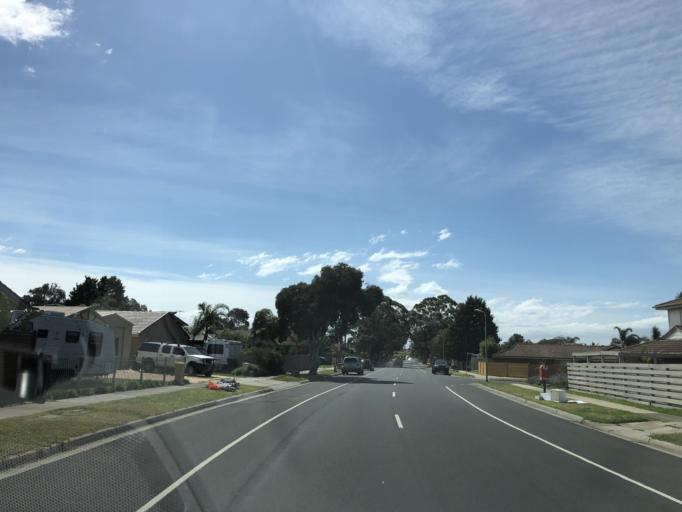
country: AU
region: Victoria
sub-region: Kingston
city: Patterson Lakes
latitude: -38.0736
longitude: 145.1452
